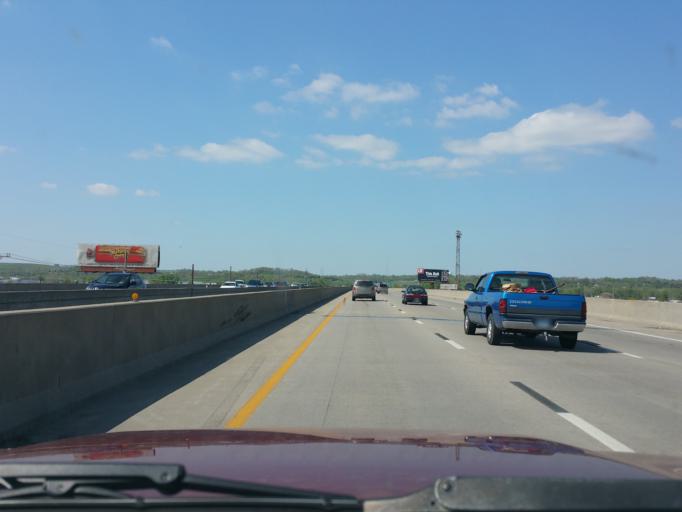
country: US
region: Kansas
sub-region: Johnson County
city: Shawnee
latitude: 39.0842
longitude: -94.6806
